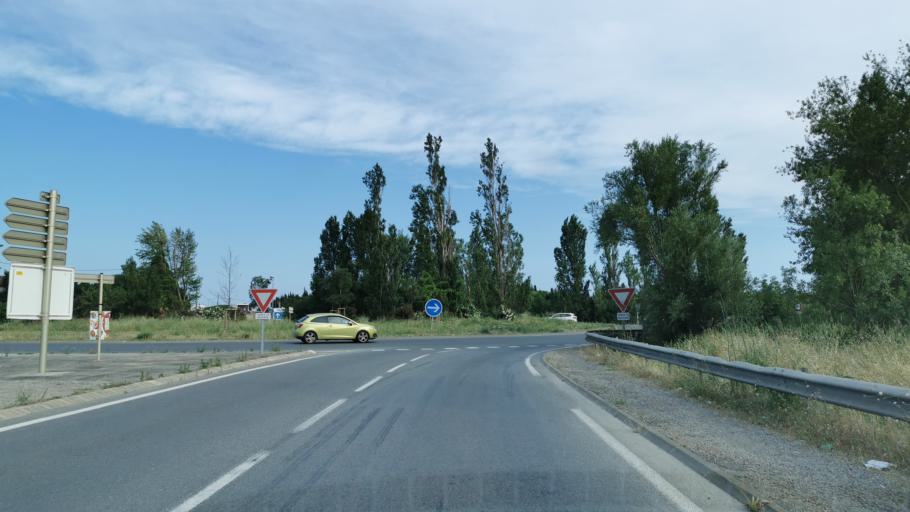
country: FR
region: Languedoc-Roussillon
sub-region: Departement de l'Aude
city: Narbonne
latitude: 43.1937
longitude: 2.9802
